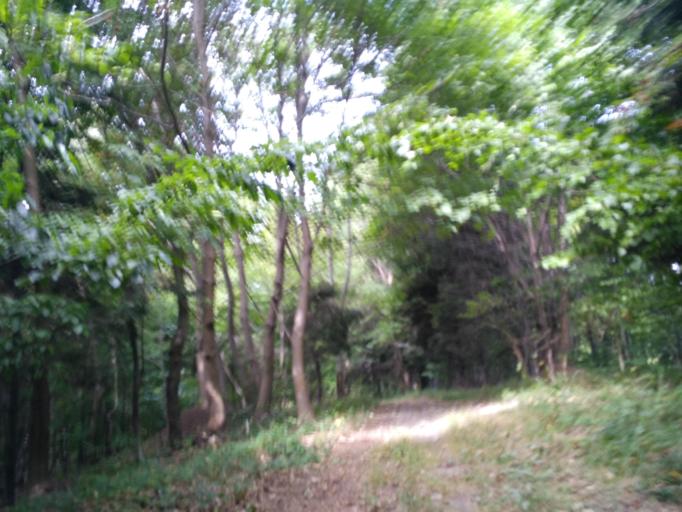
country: PL
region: Subcarpathian Voivodeship
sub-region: Powiat strzyzowski
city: Frysztak
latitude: 49.8906
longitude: 21.5549
